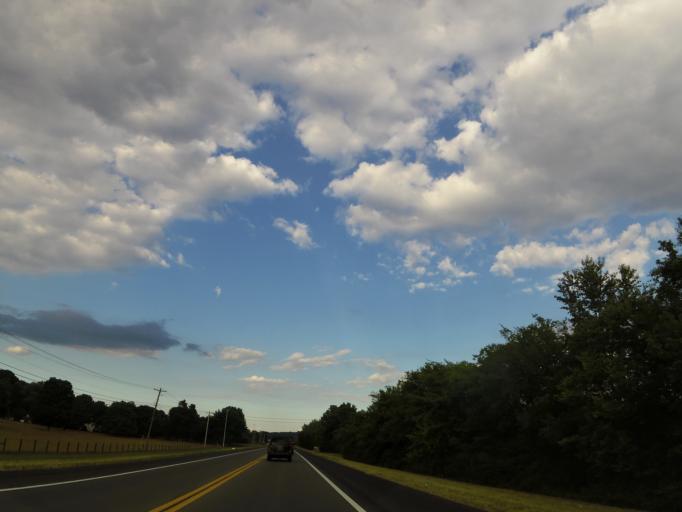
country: US
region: Tennessee
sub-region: Maury County
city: Columbia
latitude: 35.6358
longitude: -86.9847
